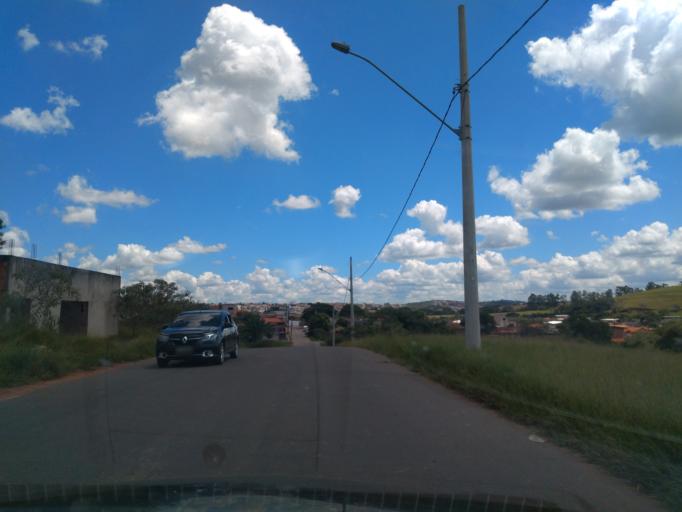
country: BR
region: Minas Gerais
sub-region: Tres Coracoes
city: Tres Coracoes
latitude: -21.6799
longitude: -45.2418
